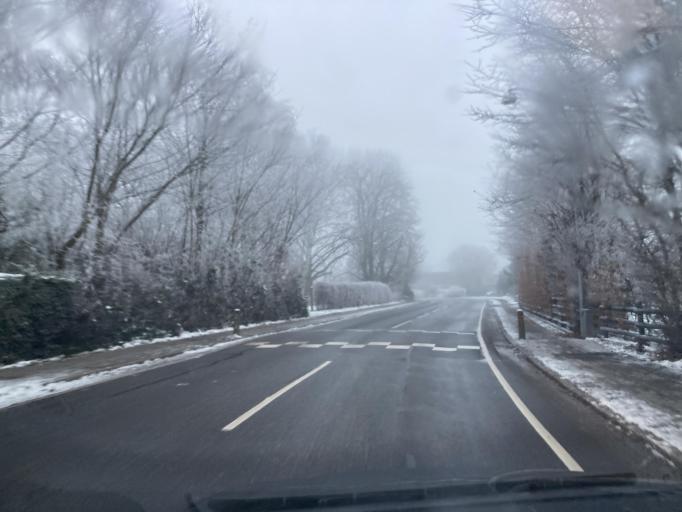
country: DK
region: Zealand
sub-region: Roskilde Kommune
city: Vindinge
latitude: 55.6267
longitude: 12.1314
